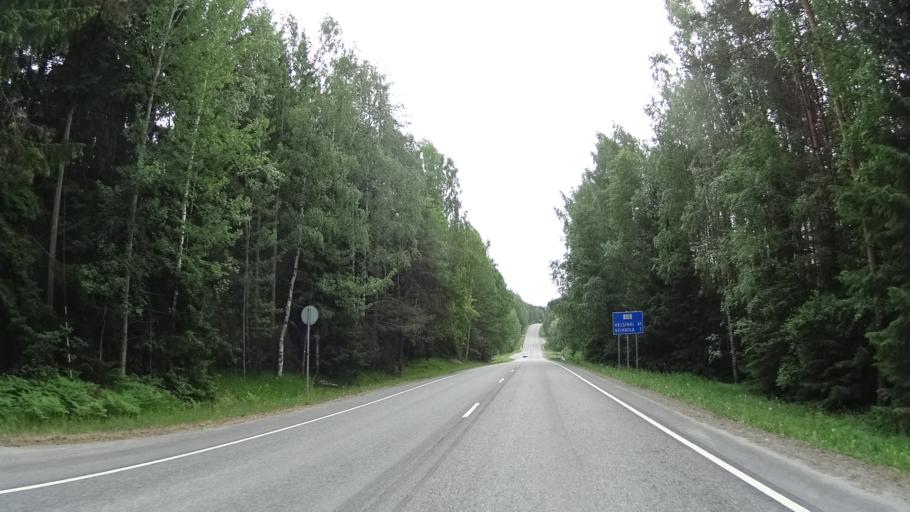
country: FI
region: Uusimaa
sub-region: Helsinki
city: Vihti
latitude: 60.3009
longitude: 24.3656
